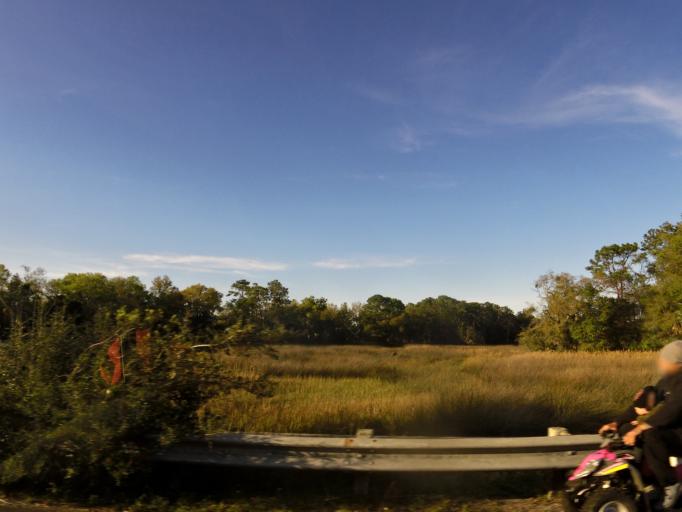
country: US
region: Florida
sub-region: Duval County
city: Jacksonville
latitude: 30.4397
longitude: -81.6262
